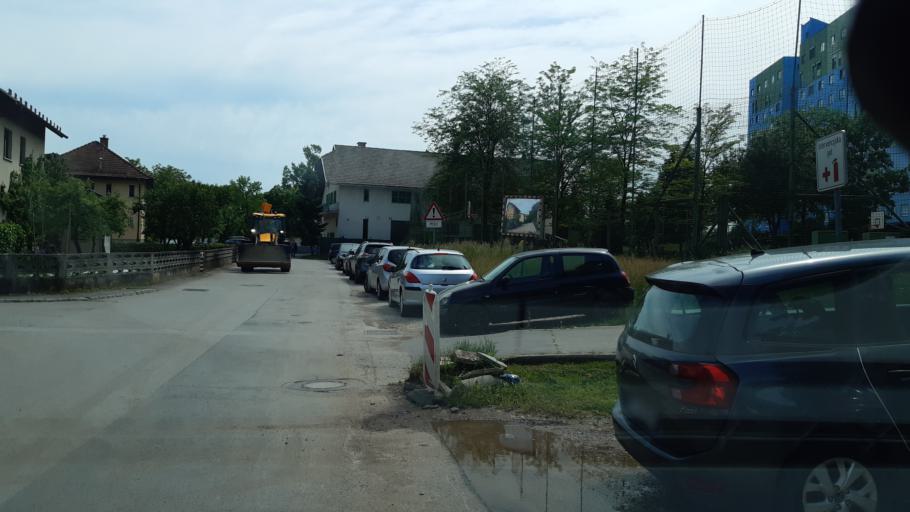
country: SI
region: Ljubljana
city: Ljubljana
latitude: 46.0843
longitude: 14.4724
